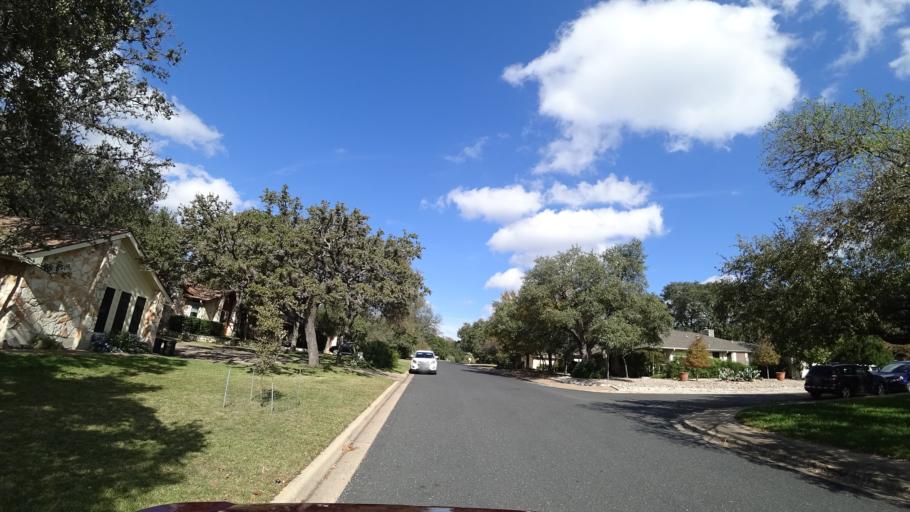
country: US
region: Texas
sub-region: Williamson County
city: Anderson Mill
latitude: 30.4234
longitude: -97.8059
